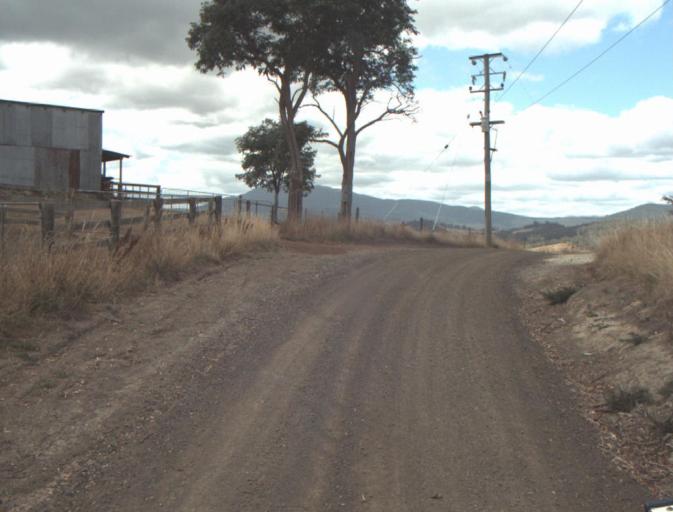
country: AU
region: Tasmania
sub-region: Launceston
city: Mayfield
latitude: -41.2069
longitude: 147.1391
